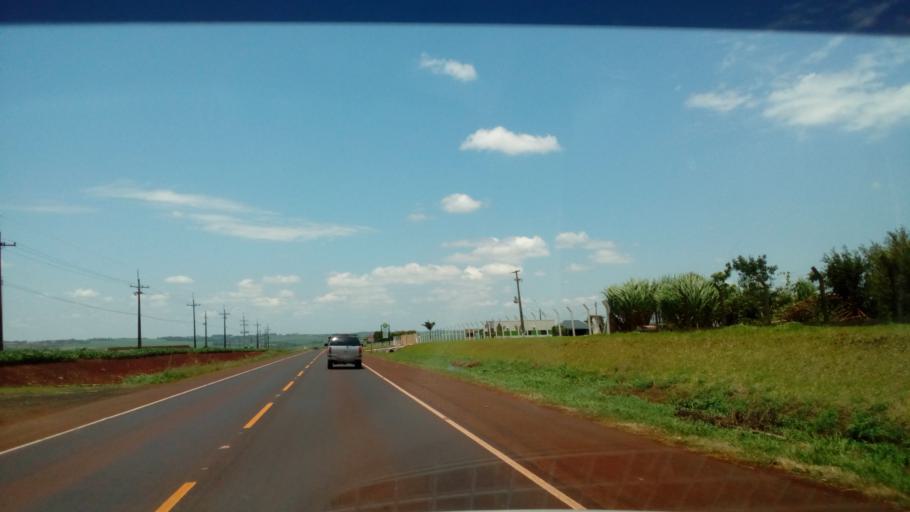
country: PY
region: Alto Parana
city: Naranjal
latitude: -25.8839
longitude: -55.1220
